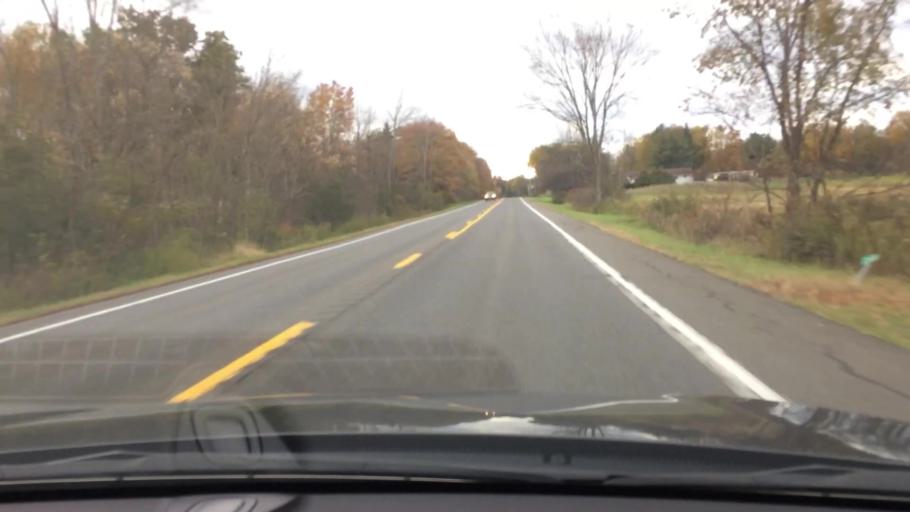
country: US
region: New York
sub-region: Columbia County
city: Kinderhook
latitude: 42.3386
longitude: -73.7046
